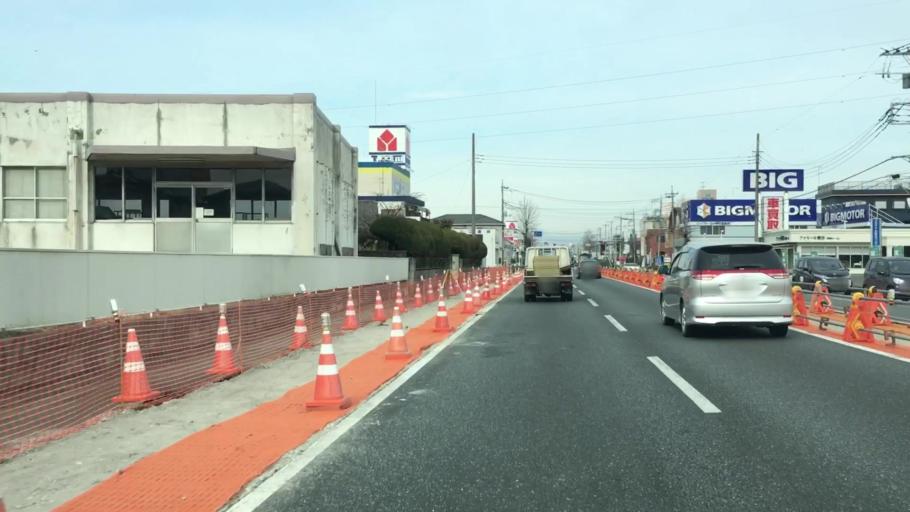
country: JP
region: Saitama
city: Kumagaya
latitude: 36.1601
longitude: 139.3709
